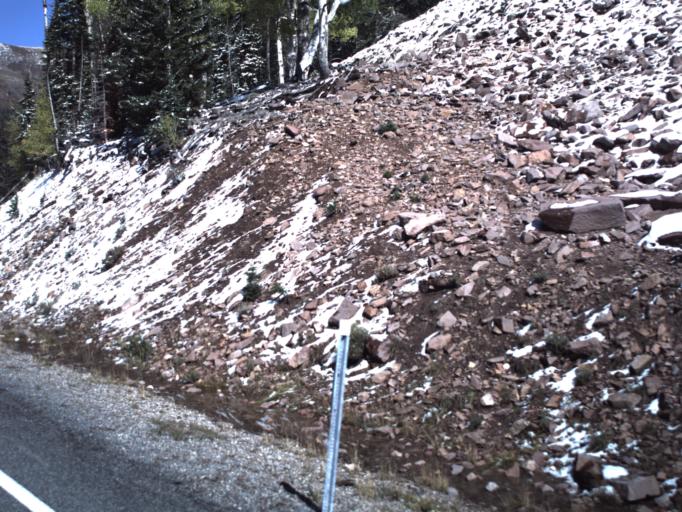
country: US
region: Utah
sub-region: Piute County
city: Junction
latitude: 38.3245
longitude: -112.3722
